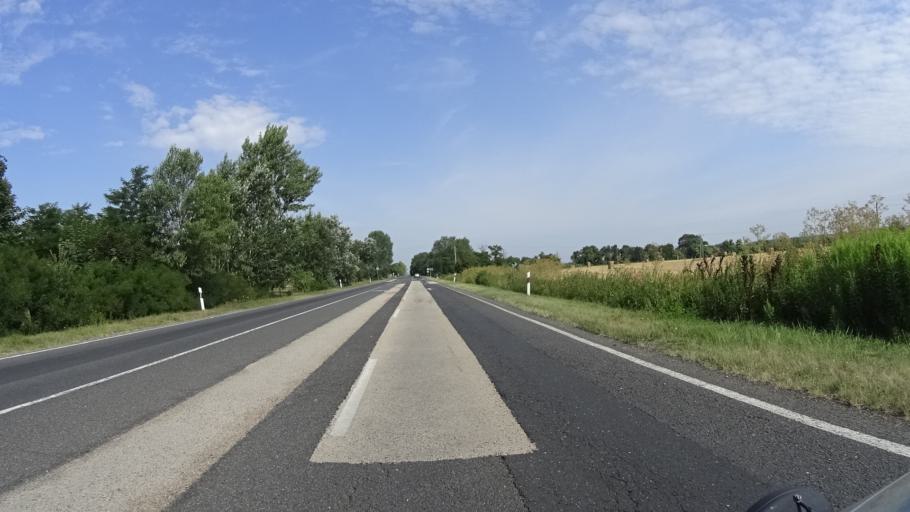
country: HU
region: Gyor-Moson-Sopron
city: Lebeny
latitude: 47.7829
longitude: 17.4130
